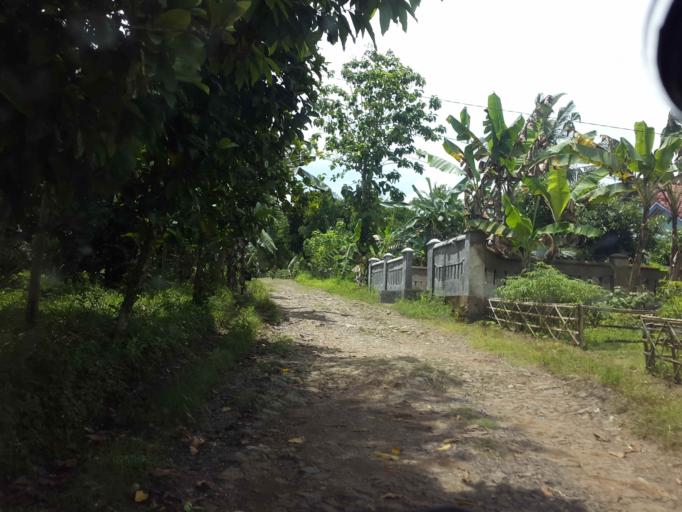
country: ID
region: Lampung
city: Sidorejo
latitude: -5.5794
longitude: 105.4547
